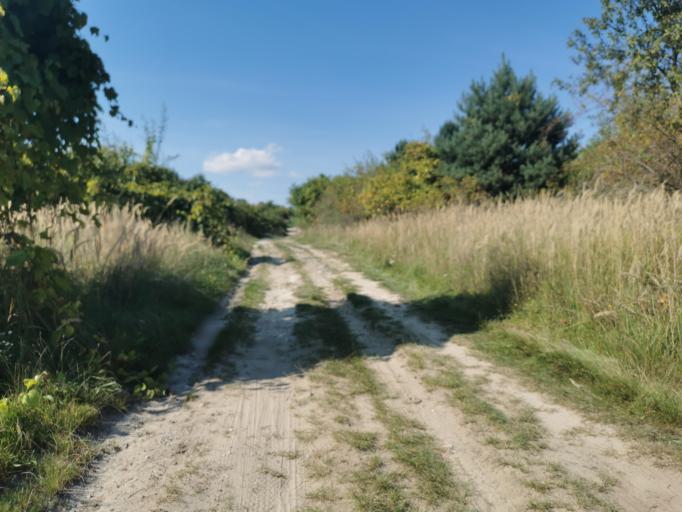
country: SK
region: Trnavsky
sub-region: Okres Senica
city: Senica
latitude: 48.6015
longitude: 17.2388
